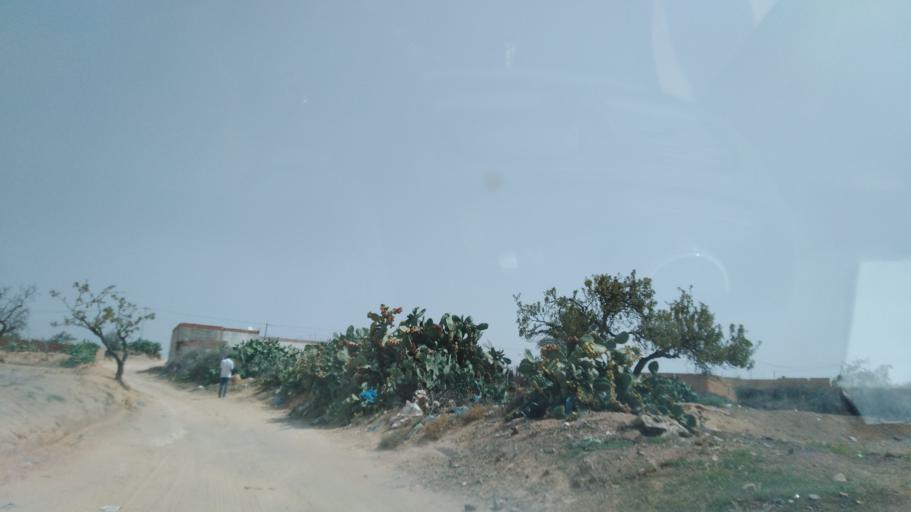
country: TN
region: Safaqis
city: Sfax
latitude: 34.6601
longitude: 10.5752
